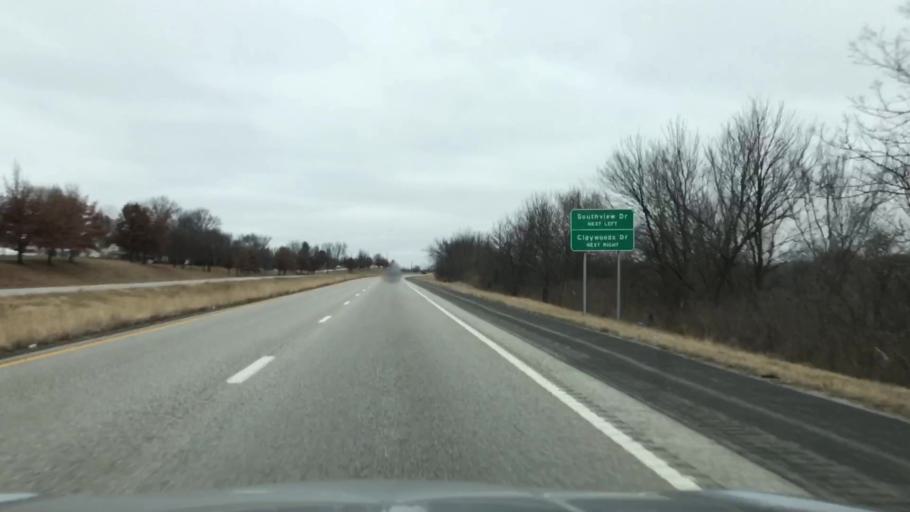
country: US
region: Missouri
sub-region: Clay County
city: Liberty
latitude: 39.2229
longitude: -94.4108
